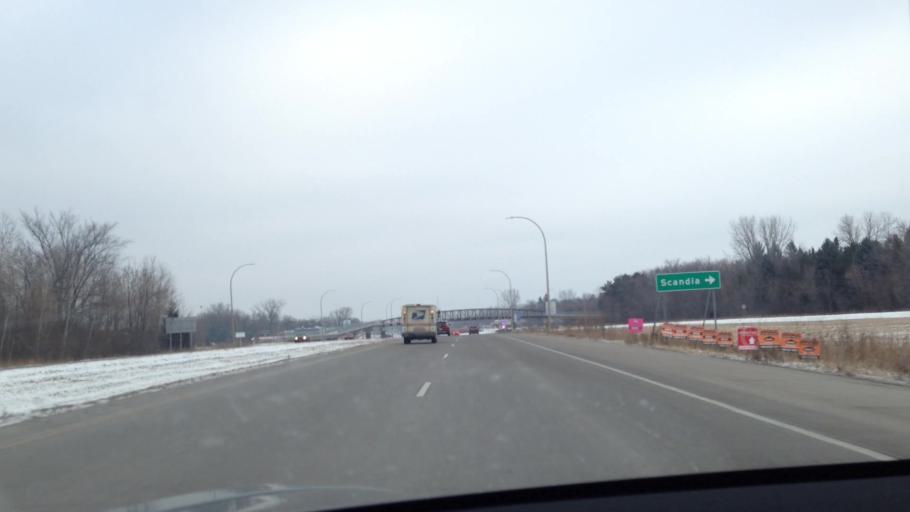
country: US
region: Minnesota
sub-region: Washington County
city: Forest Lake
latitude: 45.2565
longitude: -92.9838
